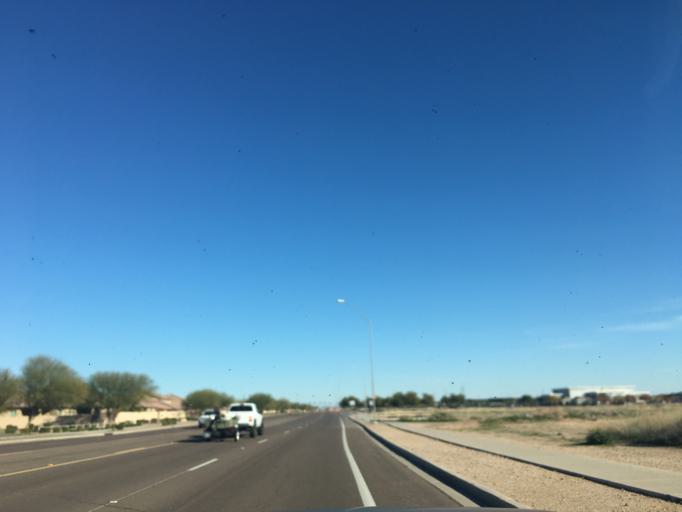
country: US
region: Arizona
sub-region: Pinal County
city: Maricopa
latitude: 33.0436
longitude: -112.0099
